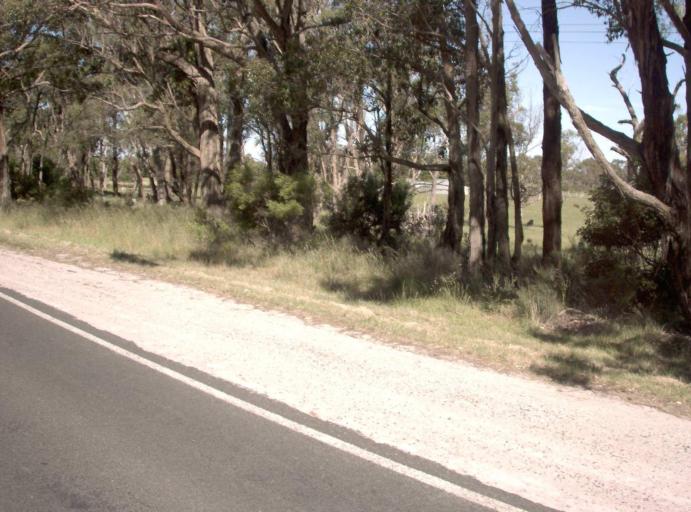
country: AU
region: Victoria
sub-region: Latrobe
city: Morwell
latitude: -38.6465
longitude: 146.4751
